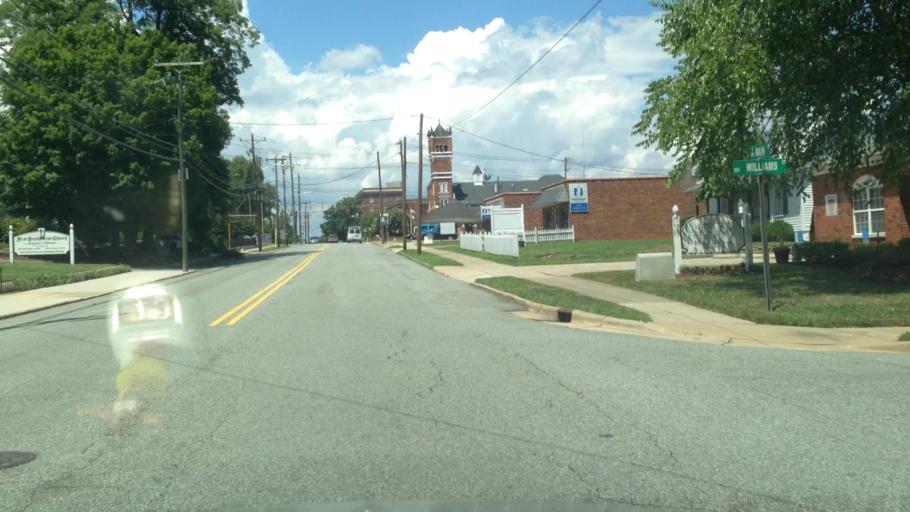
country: US
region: North Carolina
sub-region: Rockingham County
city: Reidsville
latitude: 36.3575
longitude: -79.6660
